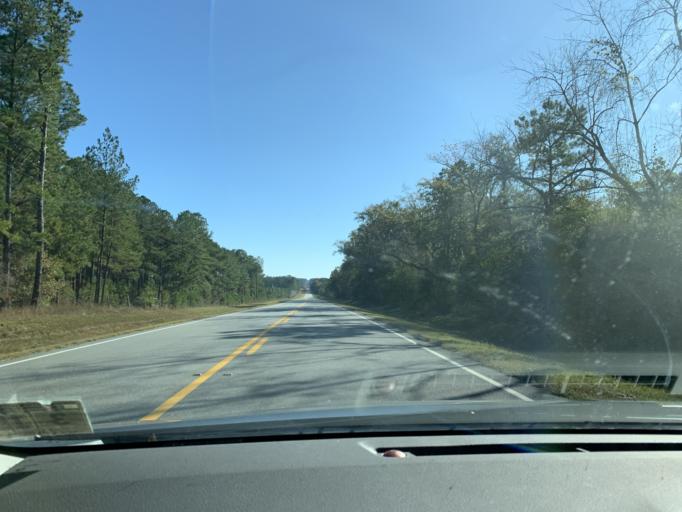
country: US
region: Georgia
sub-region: Ben Hill County
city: Fitzgerald
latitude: 31.7769
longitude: -83.0721
